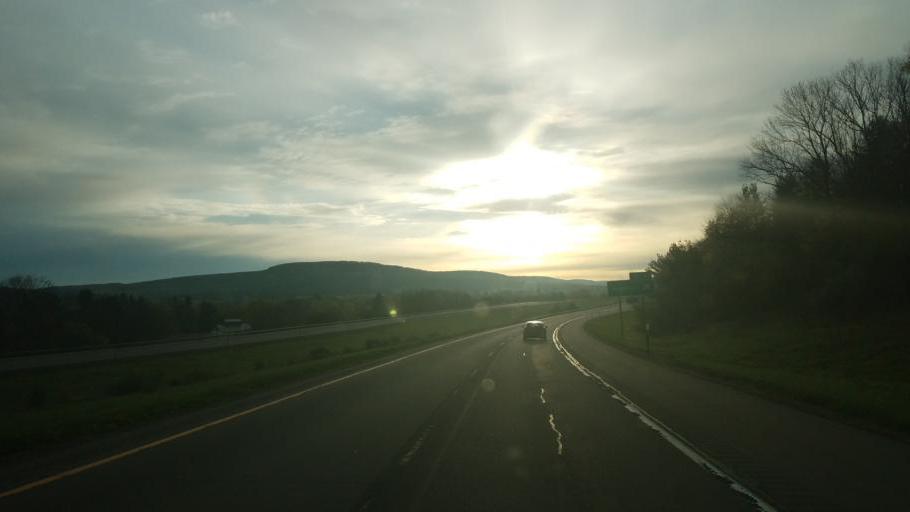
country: US
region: New York
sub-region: Allegany County
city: Belmont
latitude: 42.3004
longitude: -78.0221
